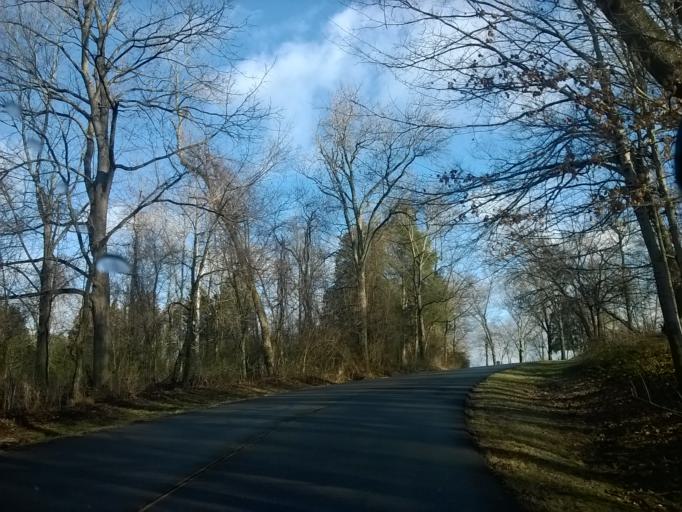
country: US
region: Indiana
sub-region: Jefferson County
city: Hanover
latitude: 38.7249
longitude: -85.4620
